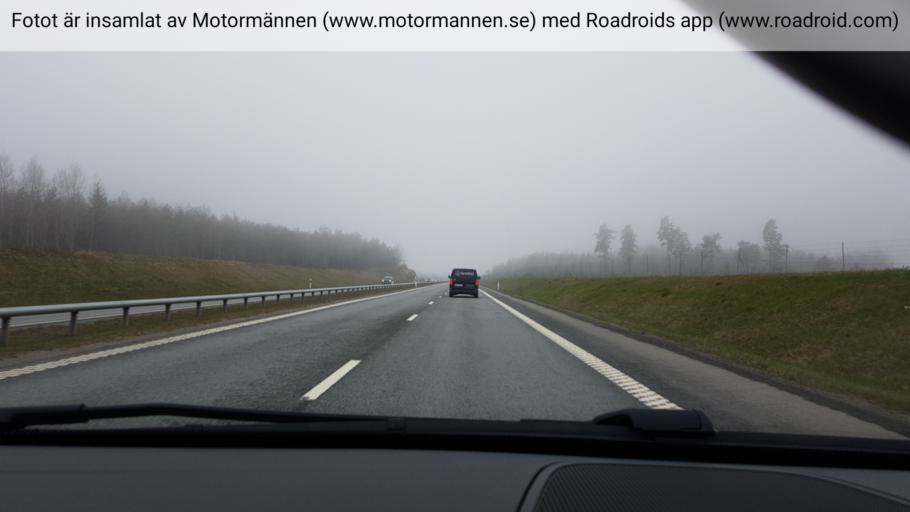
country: SE
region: Stockholm
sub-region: Haninge Kommun
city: Jordbro
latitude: 59.0932
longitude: 18.0982
